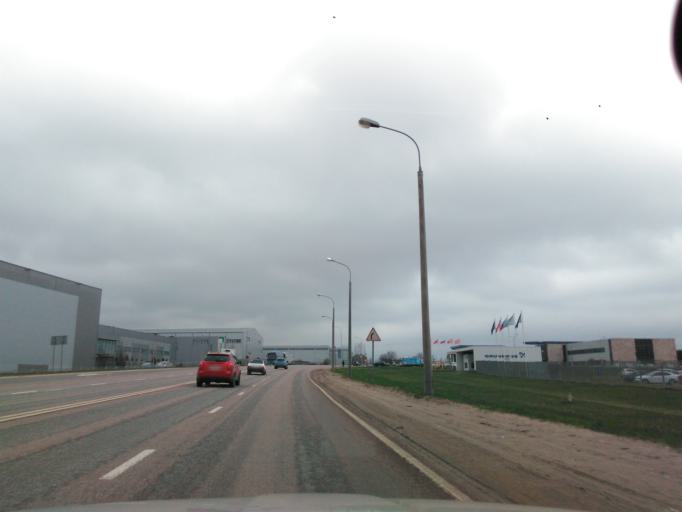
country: RU
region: Moskovskaya
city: Pavlovskaya Sloboda
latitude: 55.8186
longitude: 37.1142
